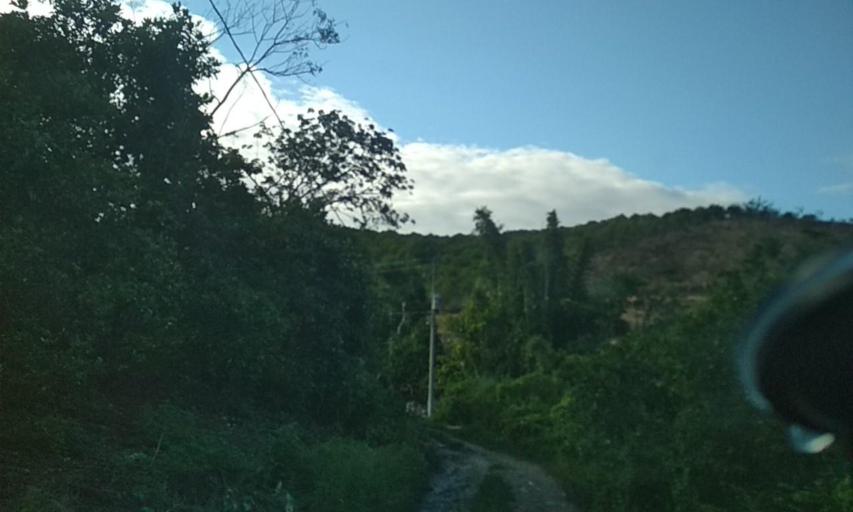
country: MX
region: Veracruz
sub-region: Papantla
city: Polutla
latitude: 20.5588
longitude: -97.2304
